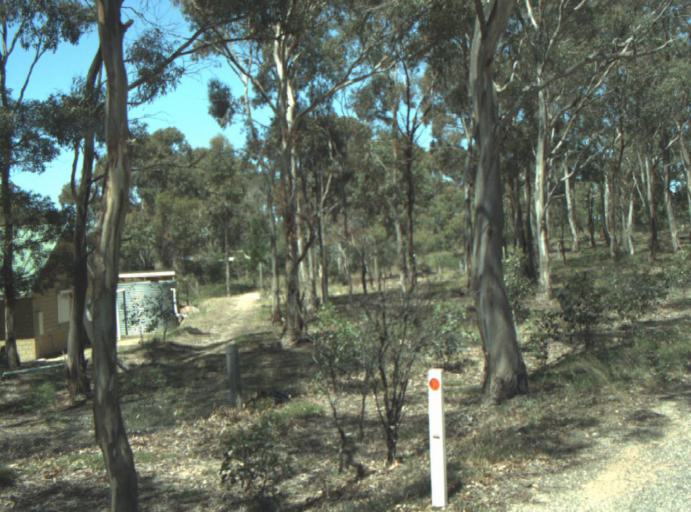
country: AU
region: Victoria
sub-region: Greater Geelong
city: Lara
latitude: -37.8376
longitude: 144.2870
